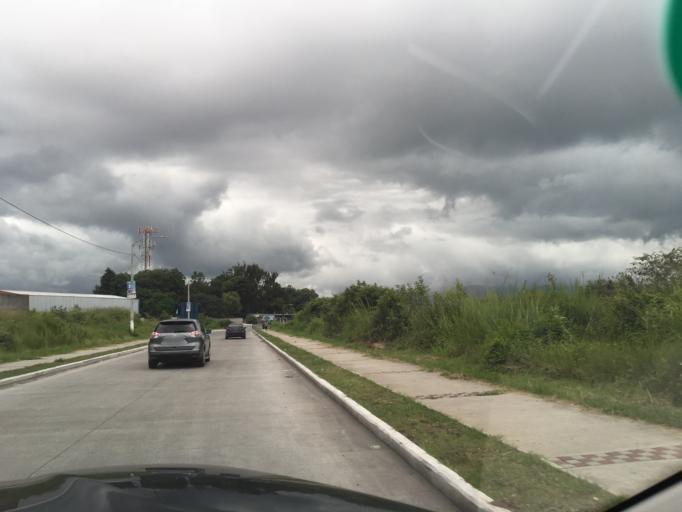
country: GT
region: Guatemala
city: Villa Nueva
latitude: 14.5081
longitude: -90.5868
